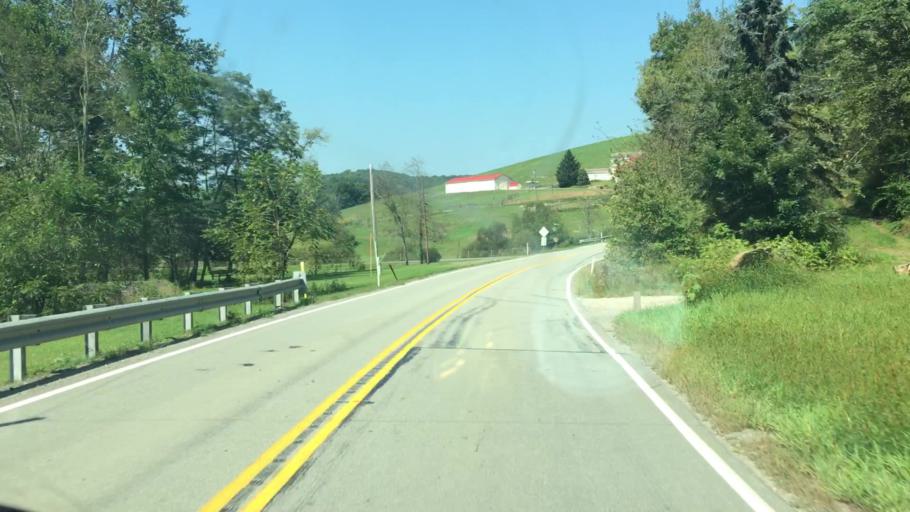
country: US
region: Pennsylvania
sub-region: Greene County
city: Waynesburg
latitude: 39.9959
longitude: -80.3536
